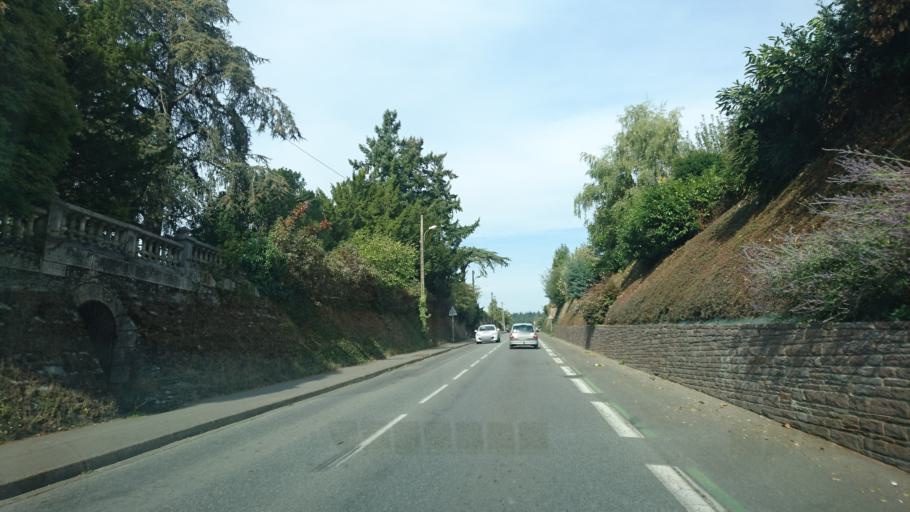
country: FR
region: Brittany
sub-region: Departement d'Ille-et-Vilaine
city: Redon
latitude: 47.6558
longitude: -2.0837
